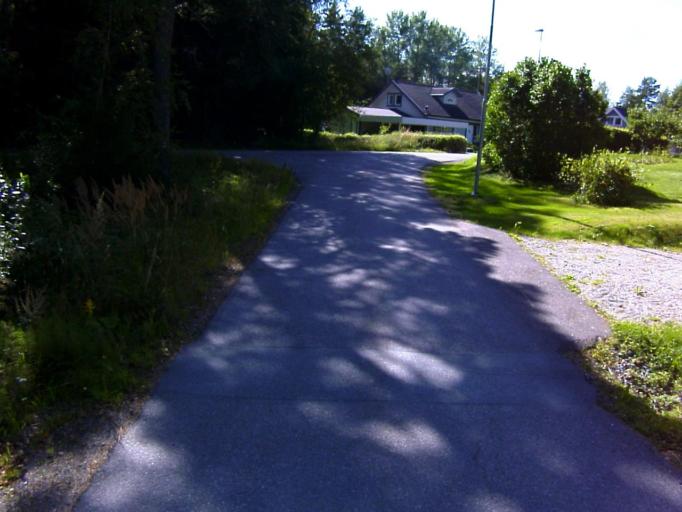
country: SE
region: Soedermanland
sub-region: Eskilstuna Kommun
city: Eskilstuna
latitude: 59.3486
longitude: 16.5730
